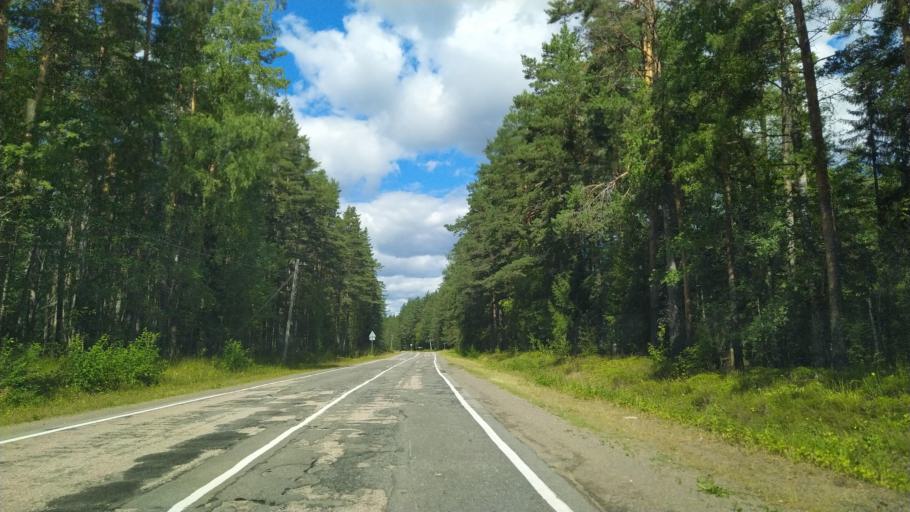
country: RU
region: Leningrad
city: Priozersk
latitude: 60.9966
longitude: 30.2510
